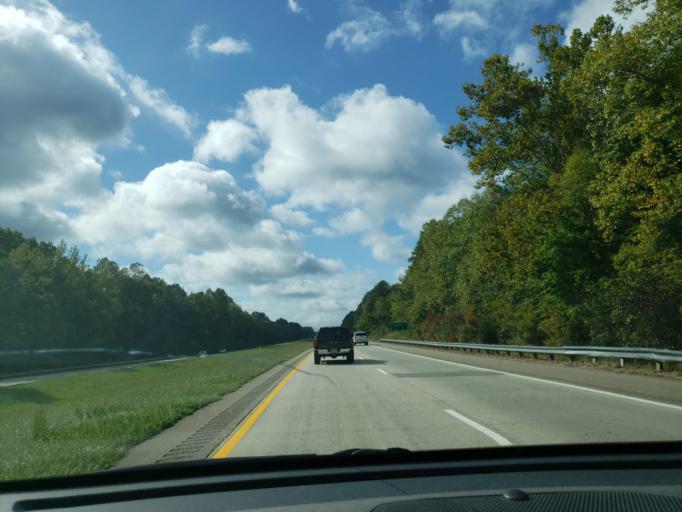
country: US
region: North Carolina
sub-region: Vance County
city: South Henderson
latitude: 36.3196
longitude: -78.4751
